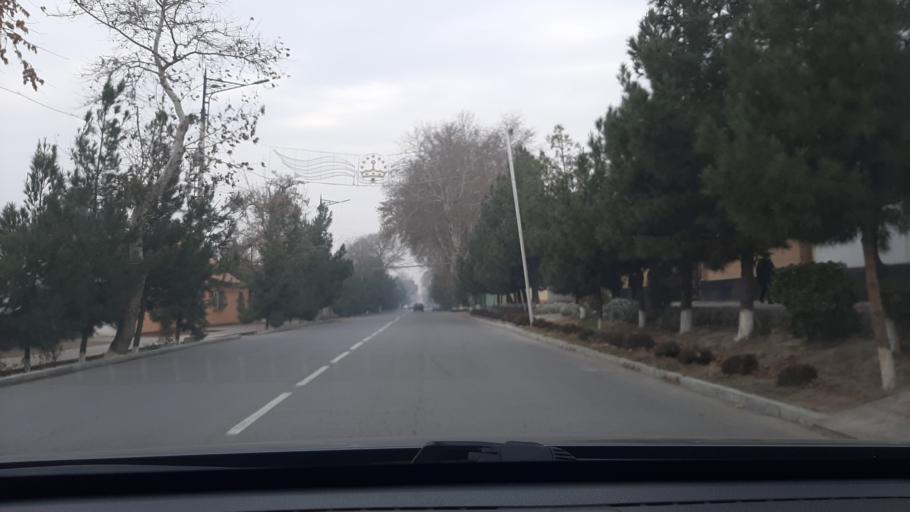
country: TJ
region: Viloyati Sughd
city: Palos
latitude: 40.2681
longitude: 69.8045
